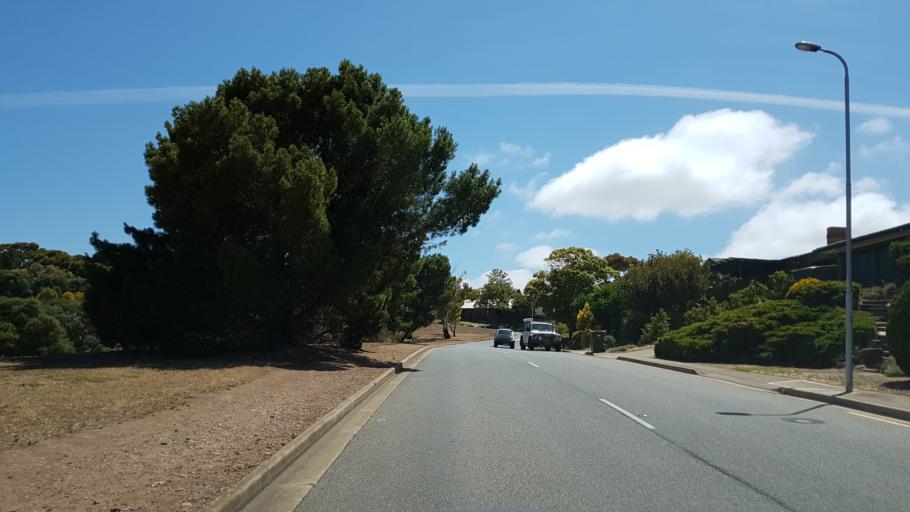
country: AU
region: South Australia
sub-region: Marion
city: Marino
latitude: -35.0681
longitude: 138.5145
